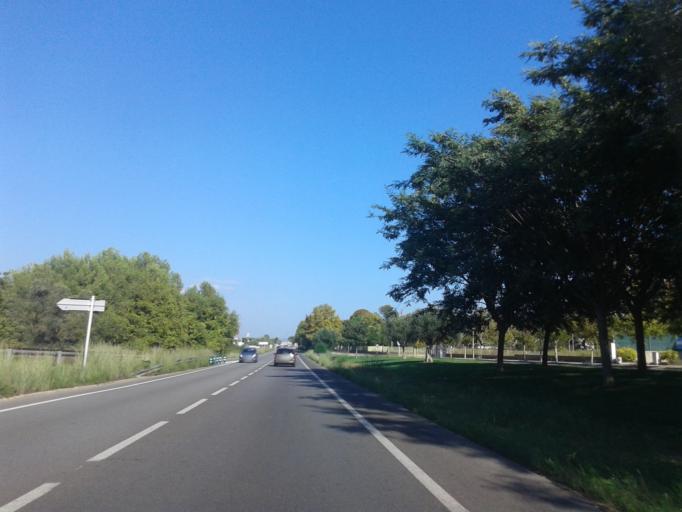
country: ES
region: Catalonia
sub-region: Provincia de Tarragona
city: Cunit
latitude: 41.2020
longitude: 1.6498
